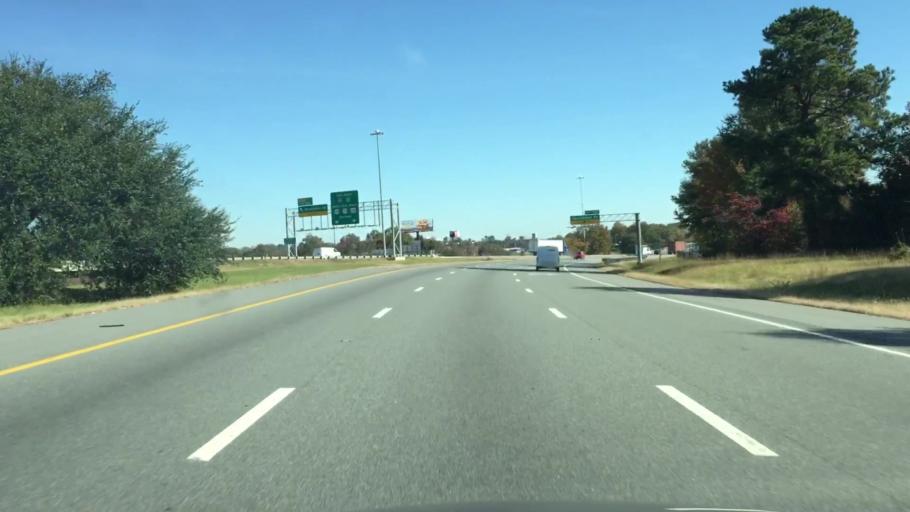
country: US
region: North Carolina
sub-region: Guilford County
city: Greensboro
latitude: 36.0310
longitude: -79.8065
